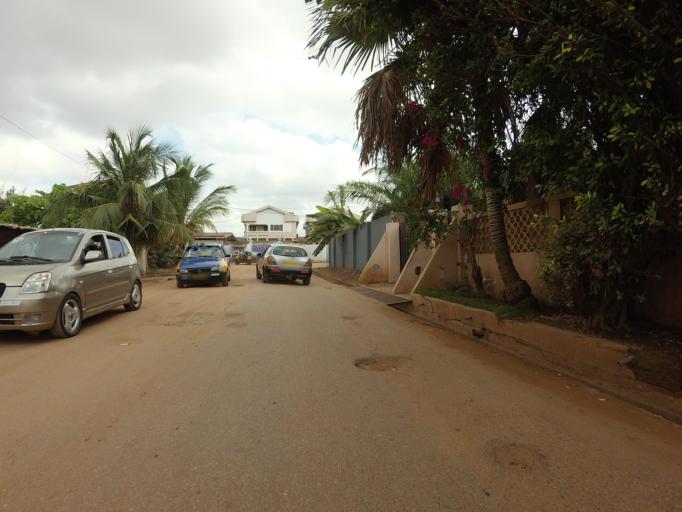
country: GH
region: Greater Accra
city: Nungua
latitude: 5.6186
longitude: -0.1011
